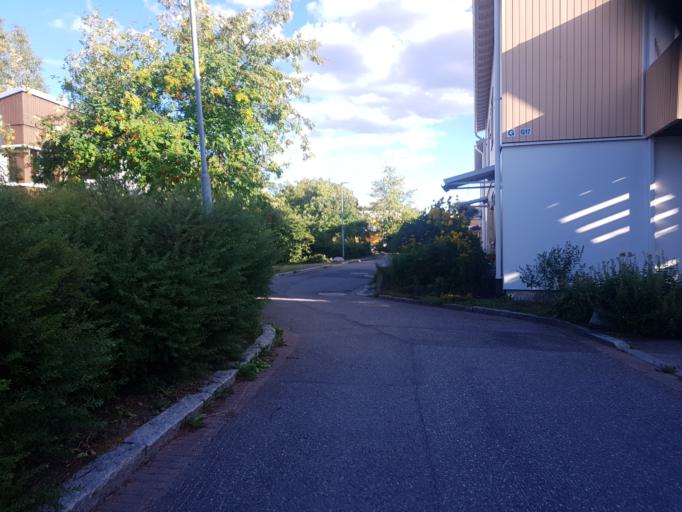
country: FI
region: Uusimaa
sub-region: Helsinki
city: Vantaa
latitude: 60.2668
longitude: 24.9825
